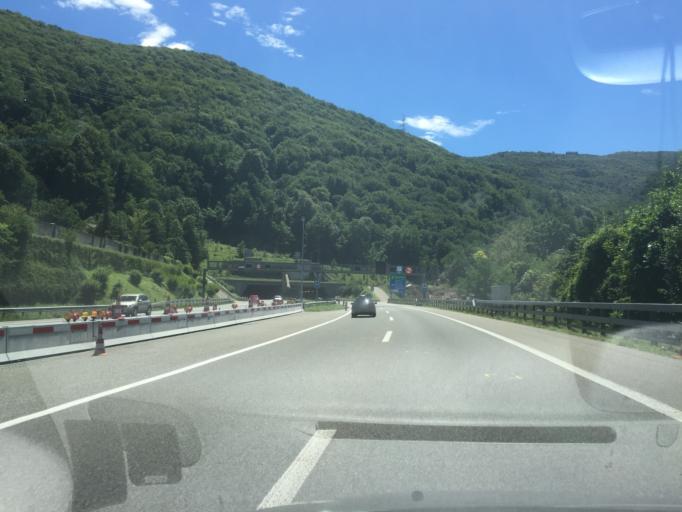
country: CH
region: Ticino
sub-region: Lugano District
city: Montagnola
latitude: 45.9662
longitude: 8.9255
